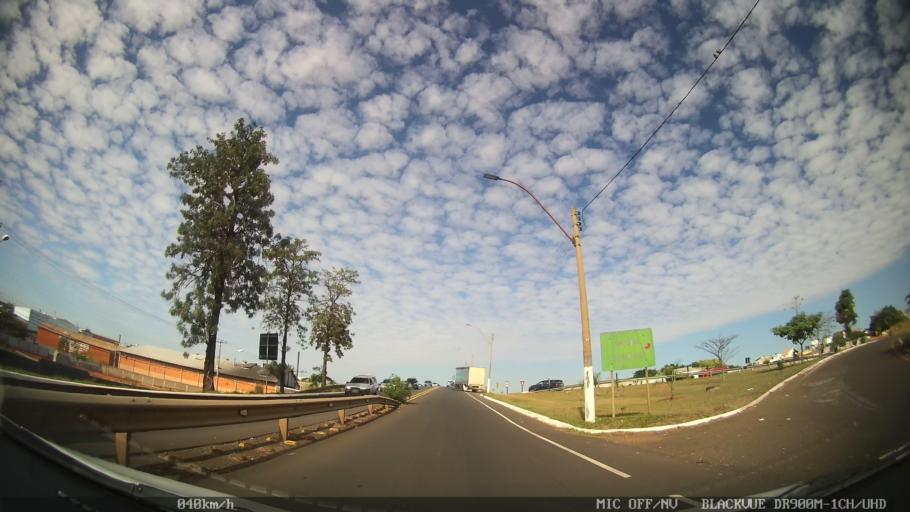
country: BR
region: Sao Paulo
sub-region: Santa Barbara D'Oeste
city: Santa Barbara d'Oeste
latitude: -22.7640
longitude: -47.3923
